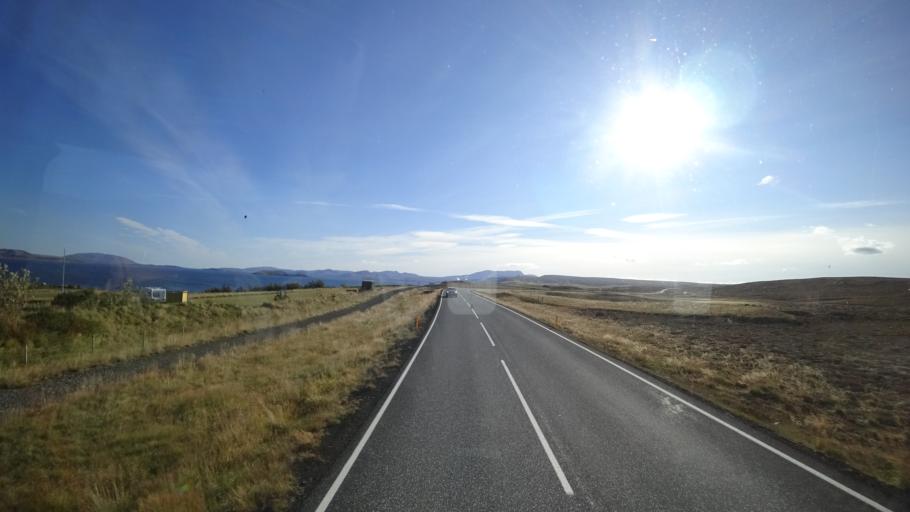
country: IS
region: South
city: Hveragerdi
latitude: 64.2321
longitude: -21.1976
